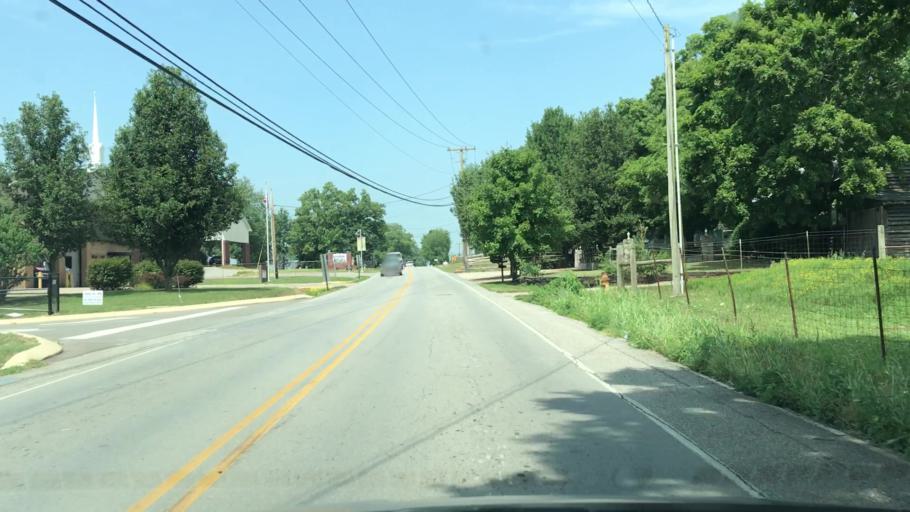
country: US
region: Tennessee
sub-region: Wilson County
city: Rural Hill
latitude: 36.1129
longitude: -86.4188
